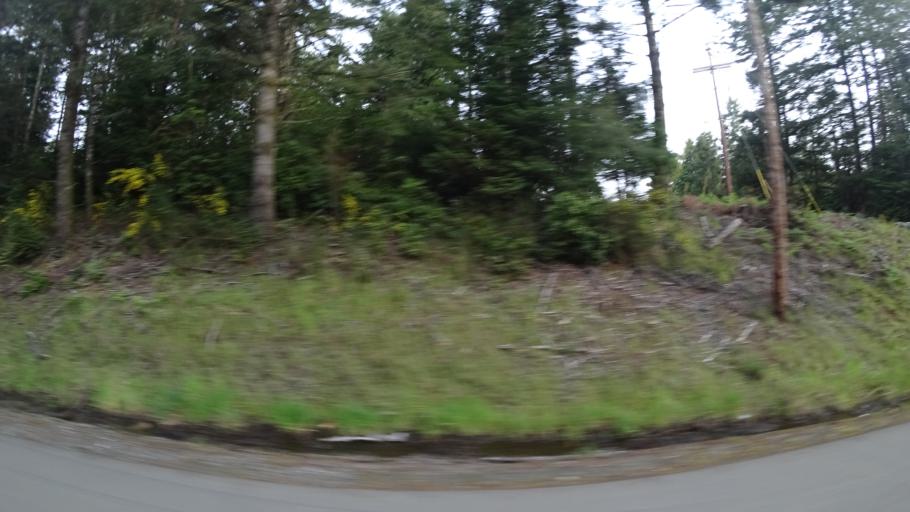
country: US
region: Oregon
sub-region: Coos County
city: Bandon
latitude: 43.1684
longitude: -124.3791
